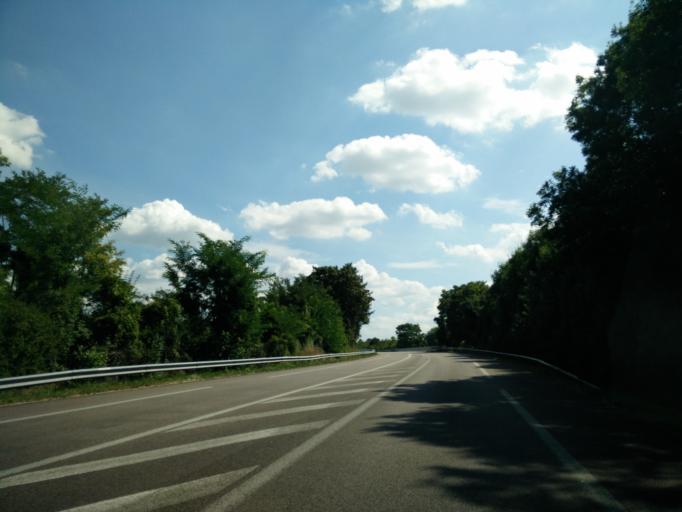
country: FR
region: Ile-de-France
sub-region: Departement des Yvelines
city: Bonnieres-sur-Seine
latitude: 49.0325
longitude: 1.5741
